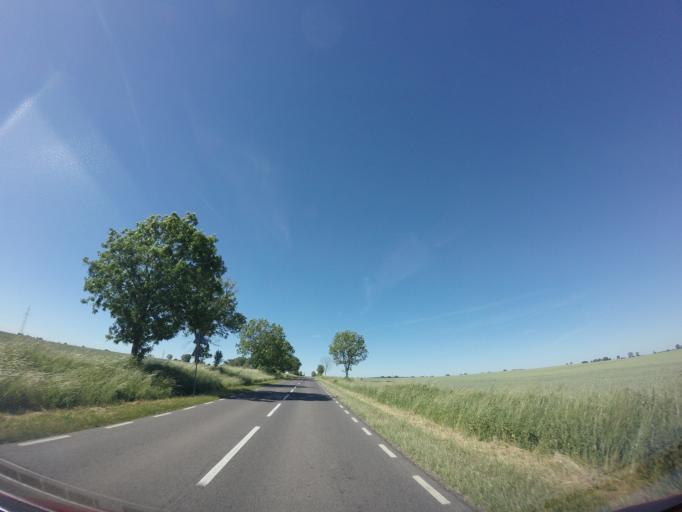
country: PL
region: West Pomeranian Voivodeship
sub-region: Powiat pyrzycki
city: Przelewice
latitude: 53.1503
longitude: 15.0305
